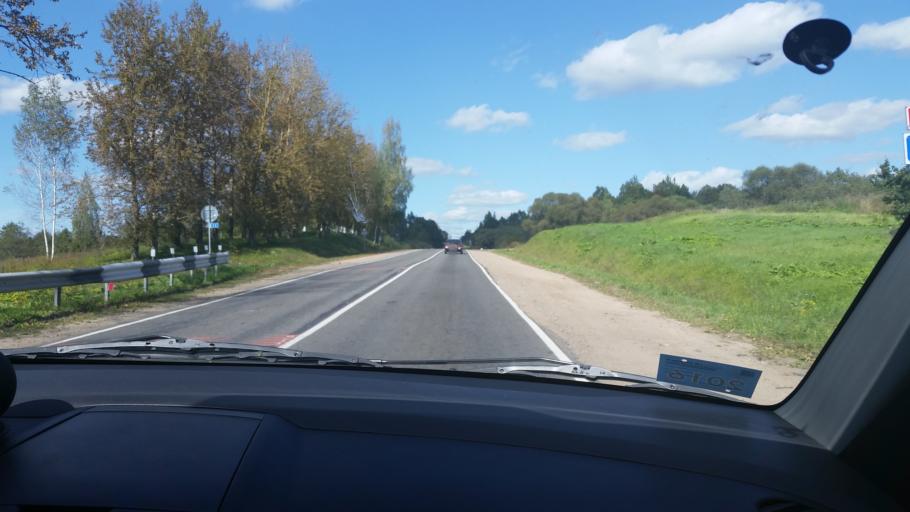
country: BY
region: Vitebsk
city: Vitebsk
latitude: 55.1039
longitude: 30.2844
